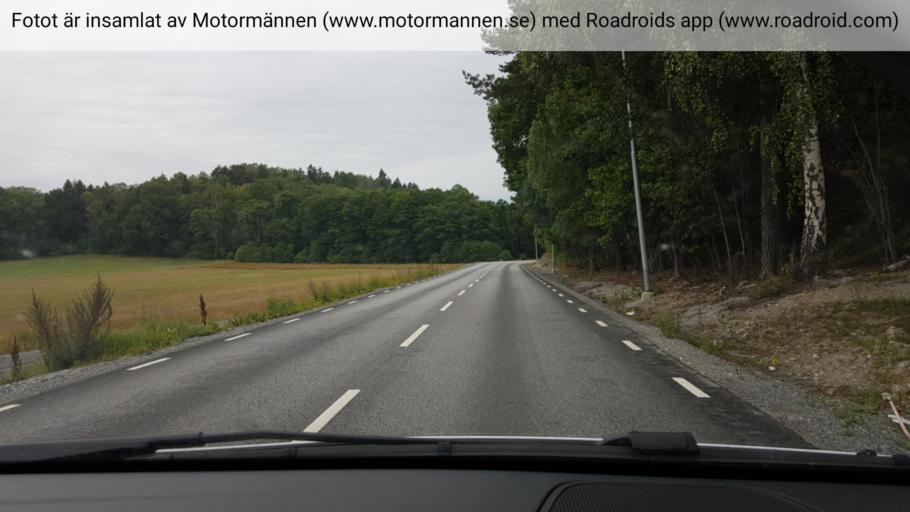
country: SE
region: Stockholm
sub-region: Botkyrka Kommun
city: Eriksberg
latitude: 59.2401
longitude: 17.8043
